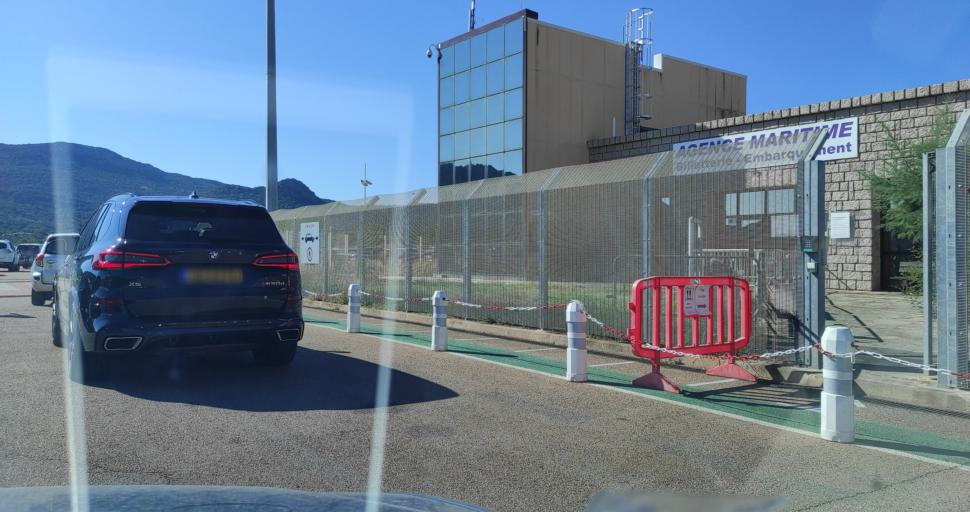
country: FR
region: Corsica
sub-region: Departement de la Corse-du-Sud
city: Porto-Vecchio
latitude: 41.5868
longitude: 9.2913
